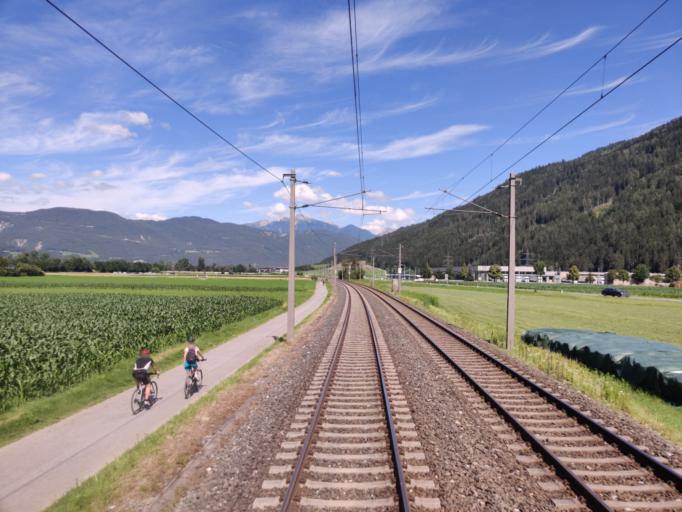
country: AT
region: Tyrol
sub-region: Politischer Bezirk Imst
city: Rietz
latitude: 47.2929
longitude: 11.0419
